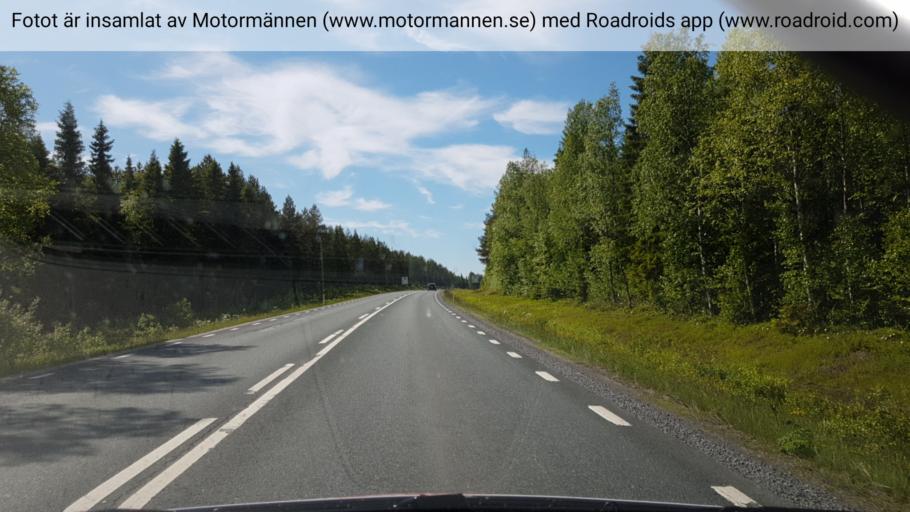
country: SE
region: Norrbotten
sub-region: Haparanda Kommun
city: Haparanda
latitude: 65.8106
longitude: 23.9974
